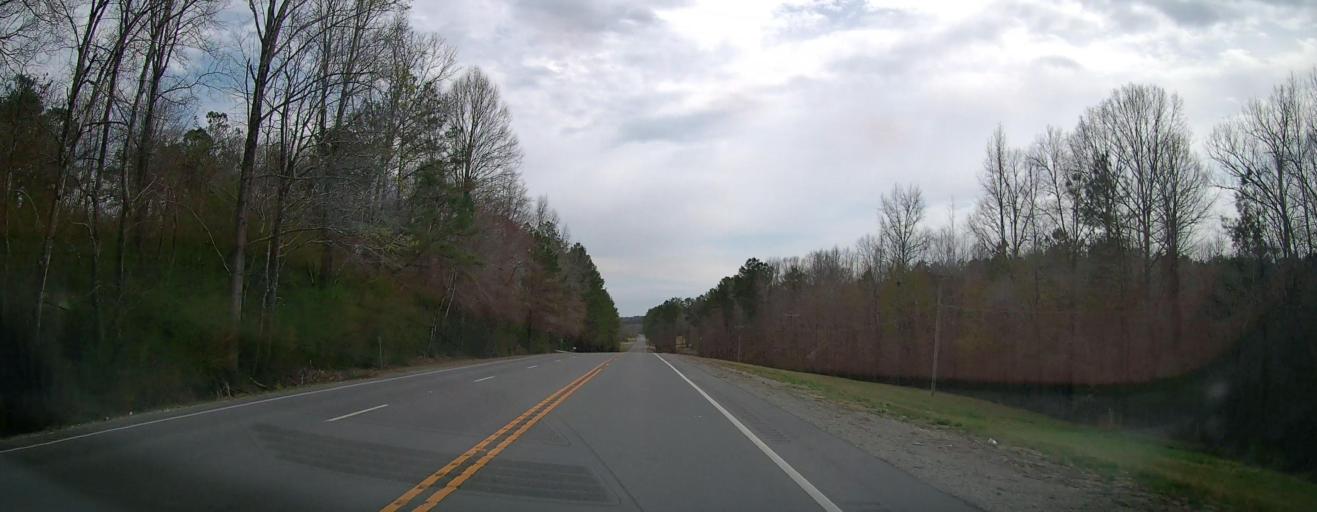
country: US
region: Alabama
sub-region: Marion County
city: Guin
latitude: 34.0162
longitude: -87.9371
